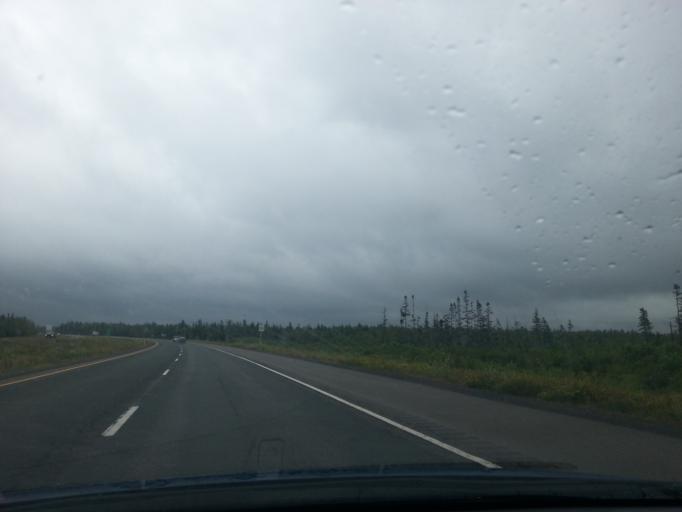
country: CA
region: New Brunswick
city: Fredericton
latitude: 45.9200
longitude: -66.7076
